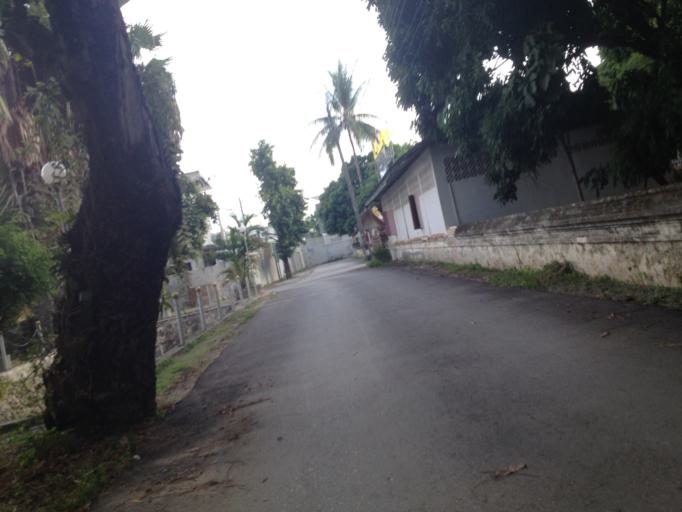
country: TH
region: Chiang Mai
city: Hang Dong
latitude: 18.7268
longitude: 98.9246
